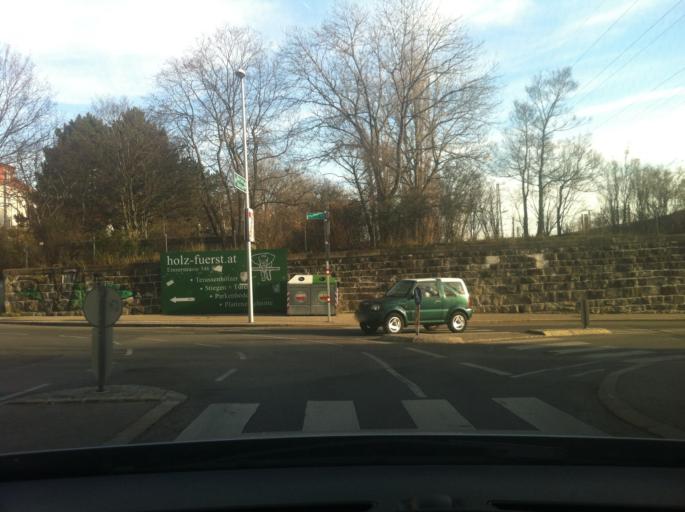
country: AT
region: Lower Austria
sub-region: Politischer Bezirk Modling
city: Perchtoldsdorf
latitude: 48.1967
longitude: 16.2668
